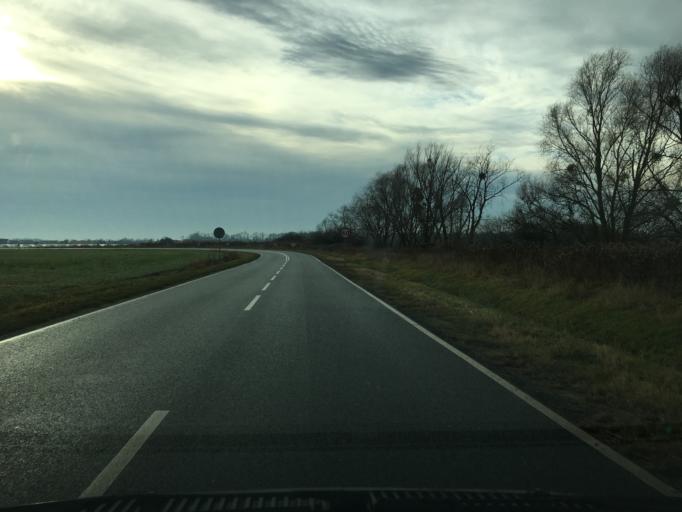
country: PL
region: Lower Silesian Voivodeship
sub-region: Powiat wroclawski
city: Dlugoleka
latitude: 51.1762
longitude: 17.2211
